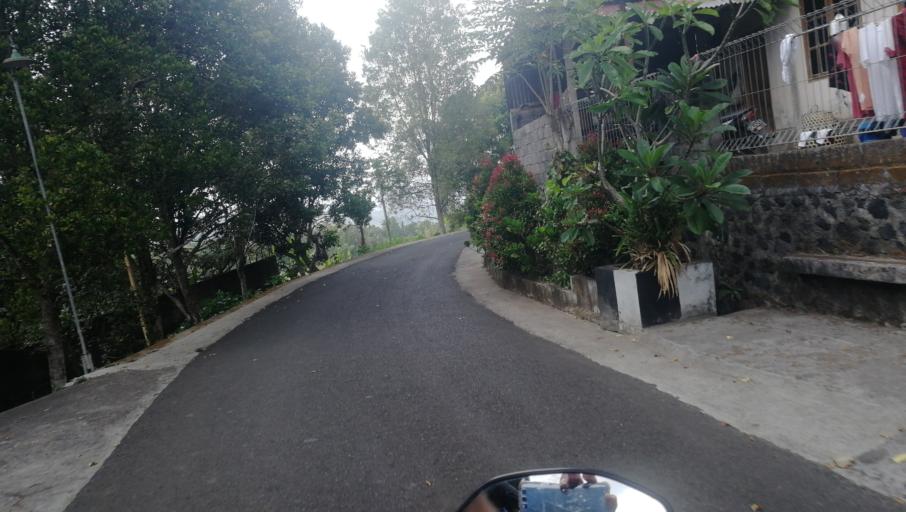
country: ID
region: Bali
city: Munduk
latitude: -8.2793
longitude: 115.0387
